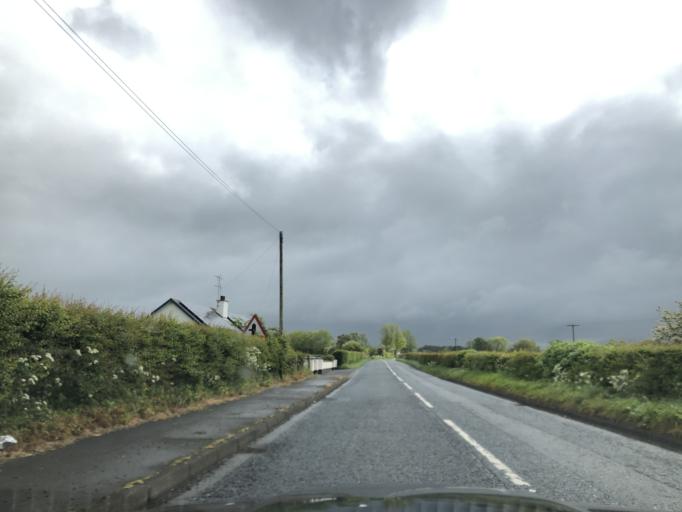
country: GB
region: Northern Ireland
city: Bushmills
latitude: 55.1574
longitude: -6.3991
